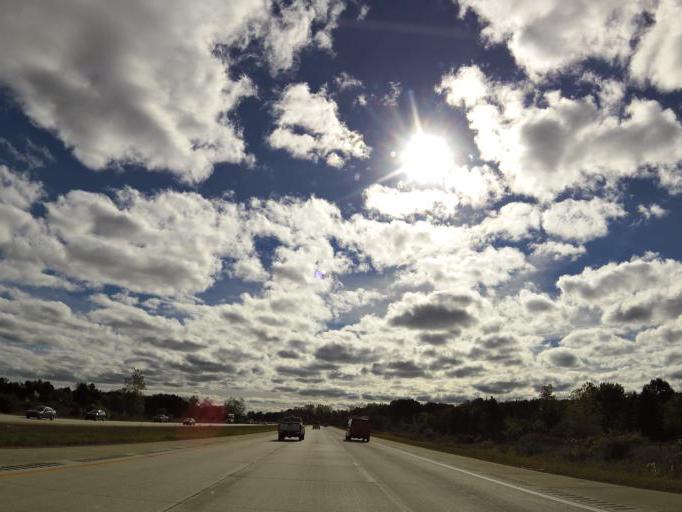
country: US
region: Michigan
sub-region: Genesee County
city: Burton
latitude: 43.0183
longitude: -83.5771
